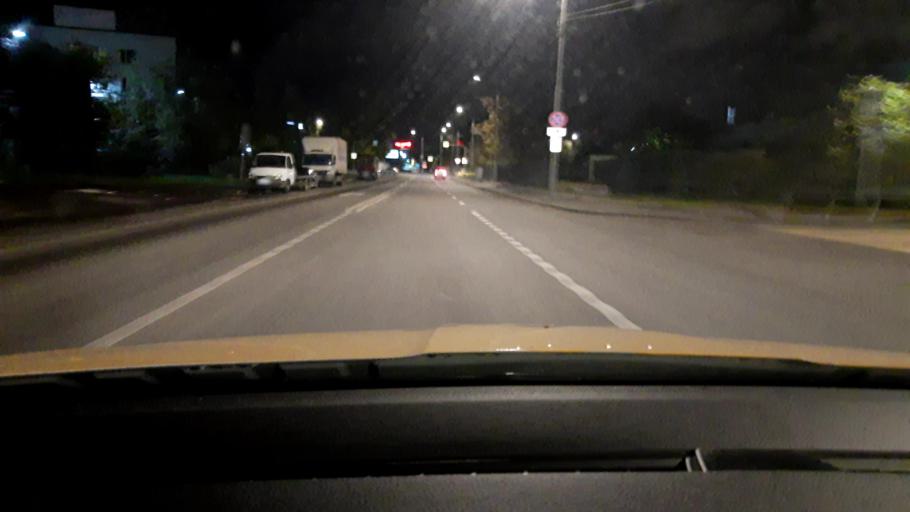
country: RU
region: Moscow
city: Vagonoremont
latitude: 55.8980
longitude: 37.5286
